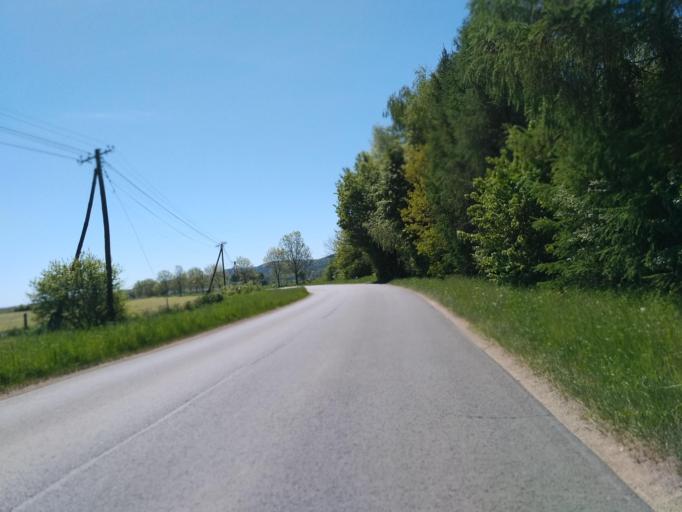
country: PL
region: Subcarpathian Voivodeship
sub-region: Powiat krosnienski
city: Sieniawa
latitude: 49.5553
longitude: 21.9366
